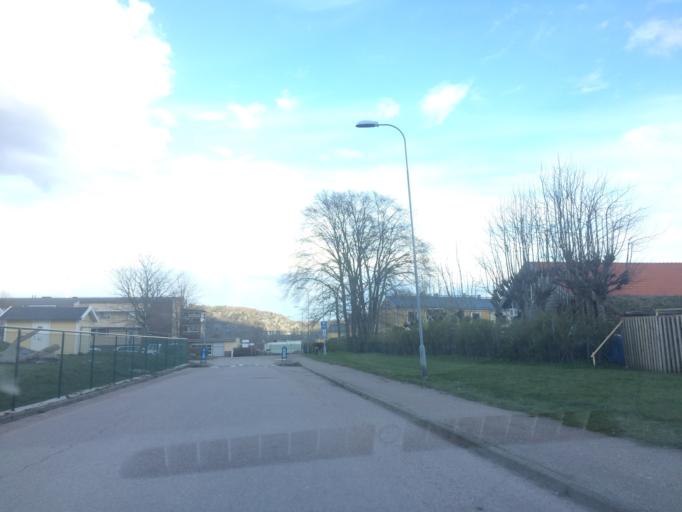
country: SE
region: Vaestra Goetaland
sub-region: Goteborg
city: Gardsten
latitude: 57.7934
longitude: 11.9938
